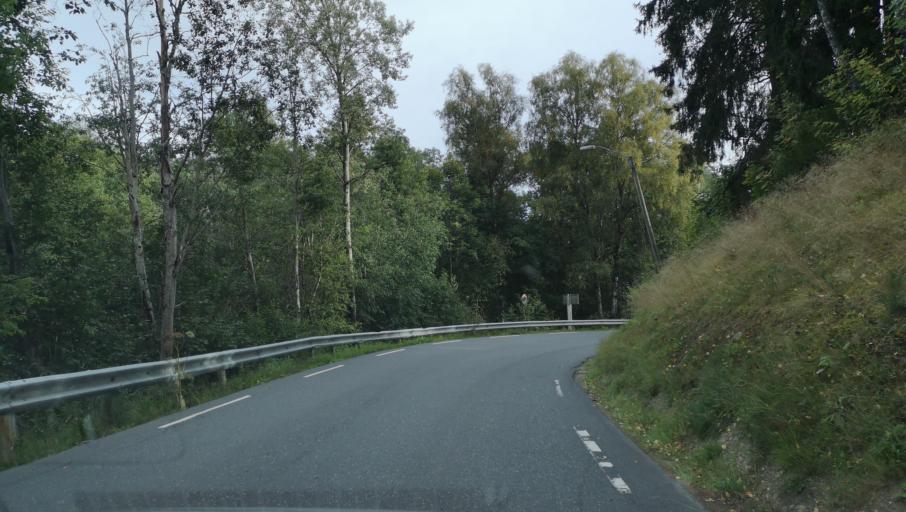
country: NO
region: Ostfold
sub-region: Hobol
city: Tomter
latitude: 59.6781
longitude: 11.0301
